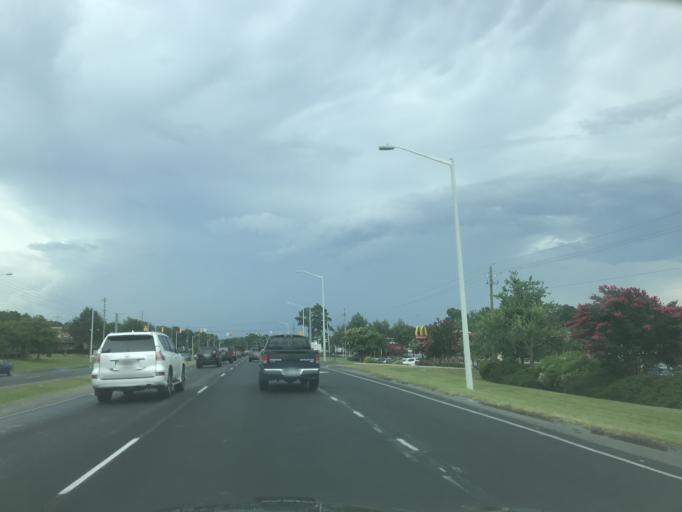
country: US
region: North Carolina
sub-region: Johnston County
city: Clayton
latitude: 35.6513
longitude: -78.4709
